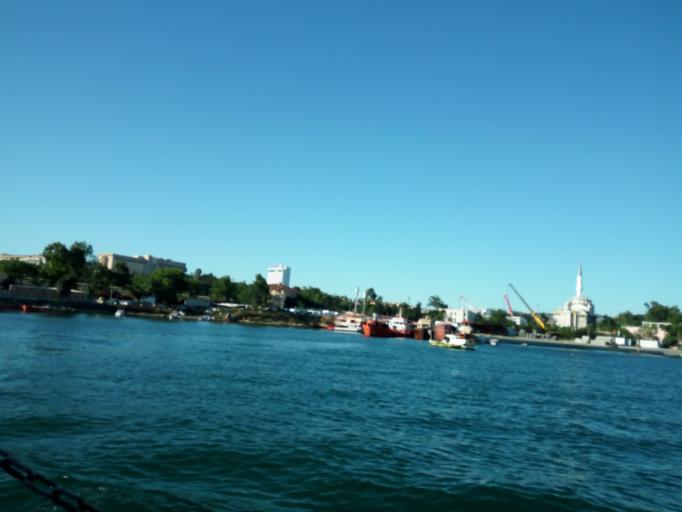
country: TR
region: Istanbul
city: UEskuedar
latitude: 40.9952
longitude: 29.0204
